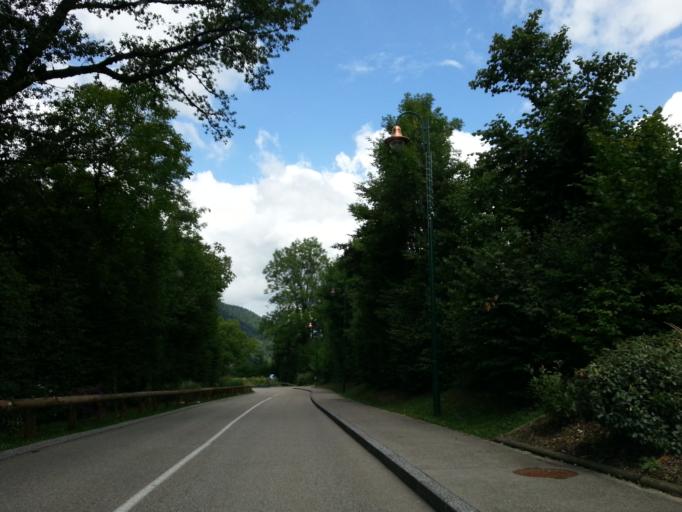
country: FR
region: Rhone-Alpes
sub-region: Departement de la Haute-Savoie
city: Menthon-Saint-Bernard
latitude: 45.8738
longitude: 6.2171
